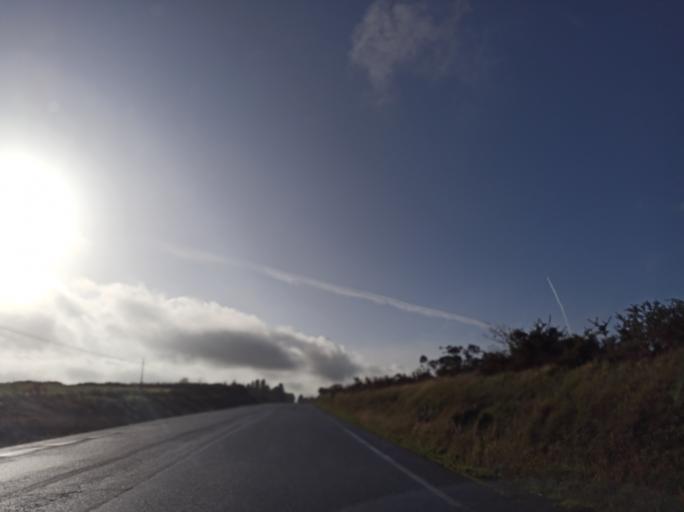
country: ES
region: Galicia
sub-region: Provincia da Coruna
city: Curtis
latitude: 43.1169
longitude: -8.0277
